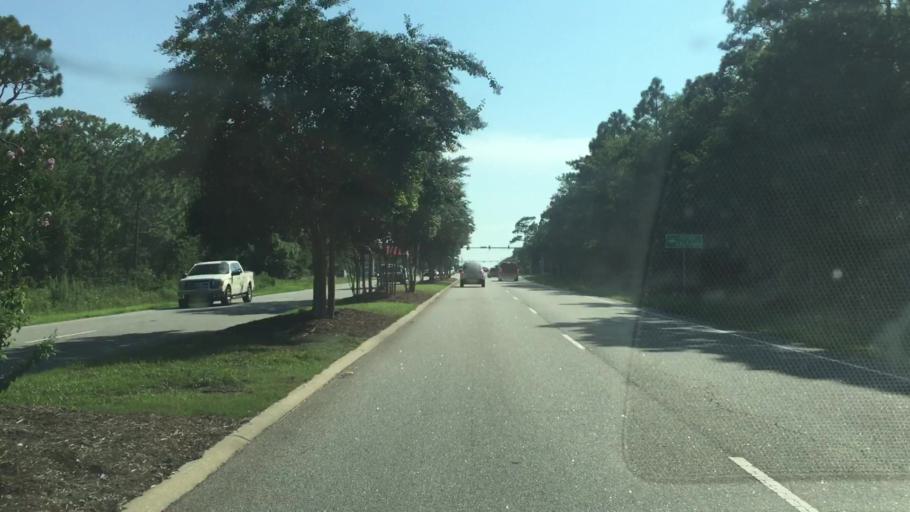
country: US
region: South Carolina
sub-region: Horry County
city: Myrtle Beach
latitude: 33.7526
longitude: -78.8121
